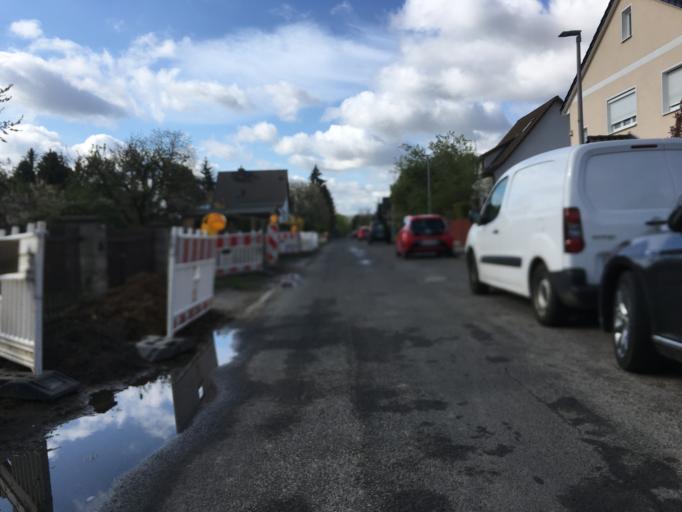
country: DE
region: Berlin
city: Biesdorf
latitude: 52.5186
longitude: 13.5351
